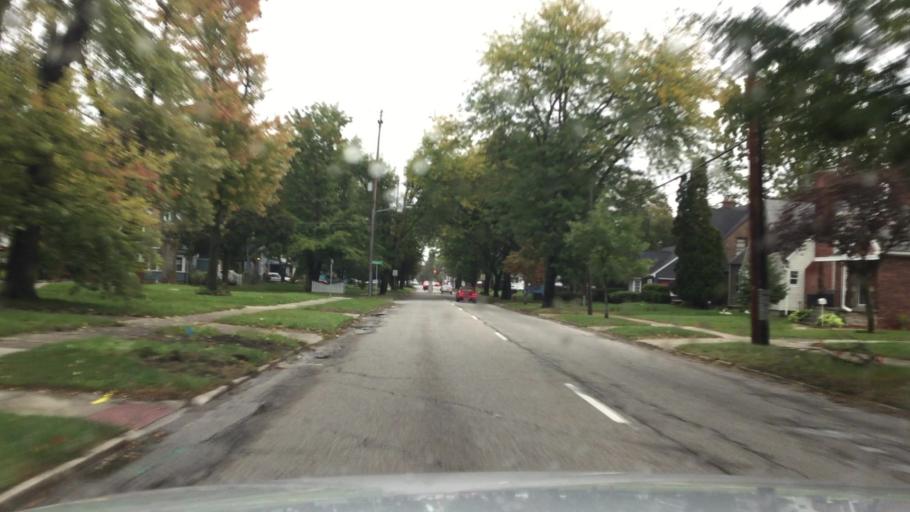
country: US
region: Michigan
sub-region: Saginaw County
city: Saginaw
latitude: 43.4367
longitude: -83.9802
